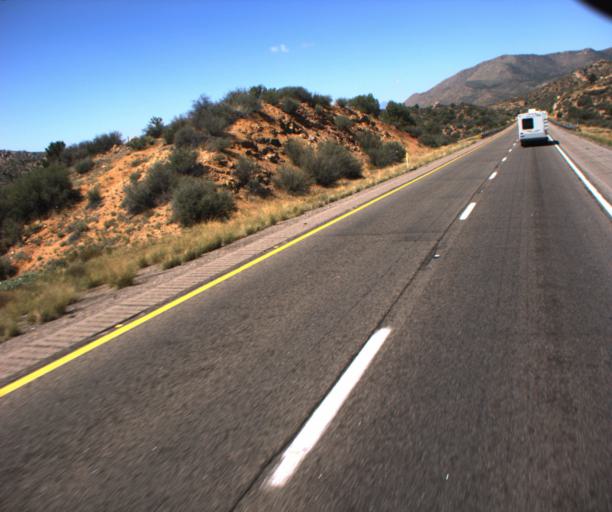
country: US
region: Arizona
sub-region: Mohave County
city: Peach Springs
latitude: 35.1790
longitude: -113.4870
